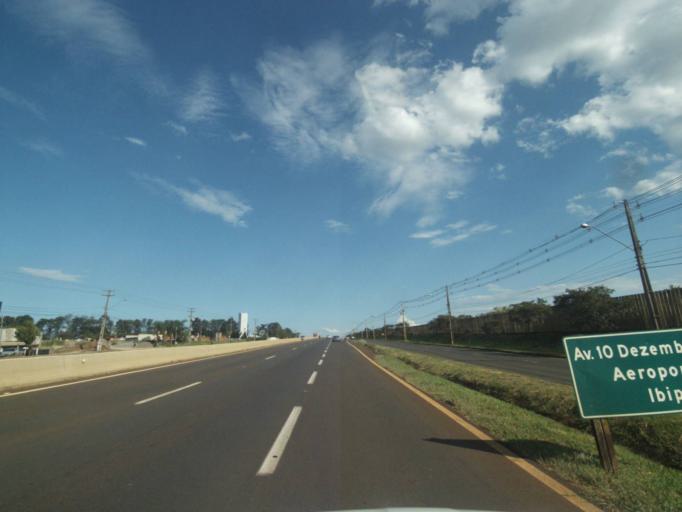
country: BR
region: Parana
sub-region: Londrina
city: Londrina
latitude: -23.3564
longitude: -51.1590
